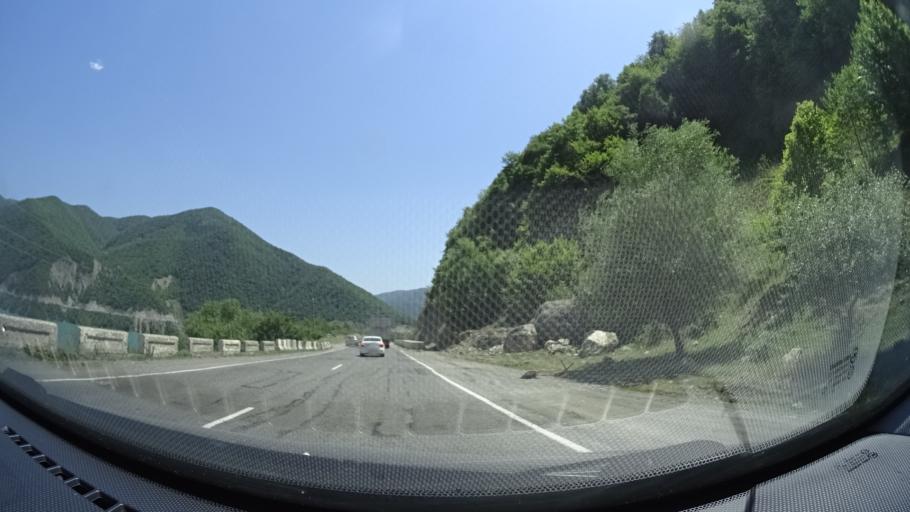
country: GE
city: Zhinvali
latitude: 42.1443
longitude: 44.7664
